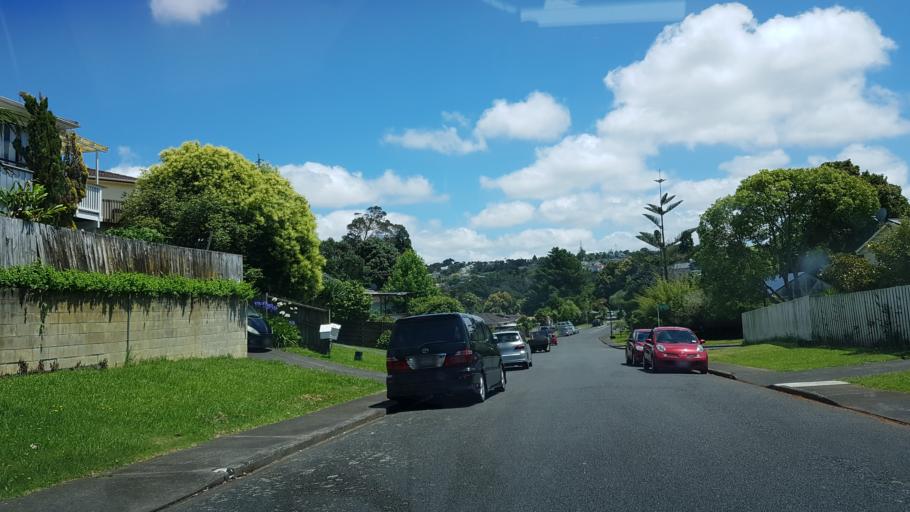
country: NZ
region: Auckland
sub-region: Auckland
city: North Shore
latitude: -36.7855
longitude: 174.7164
